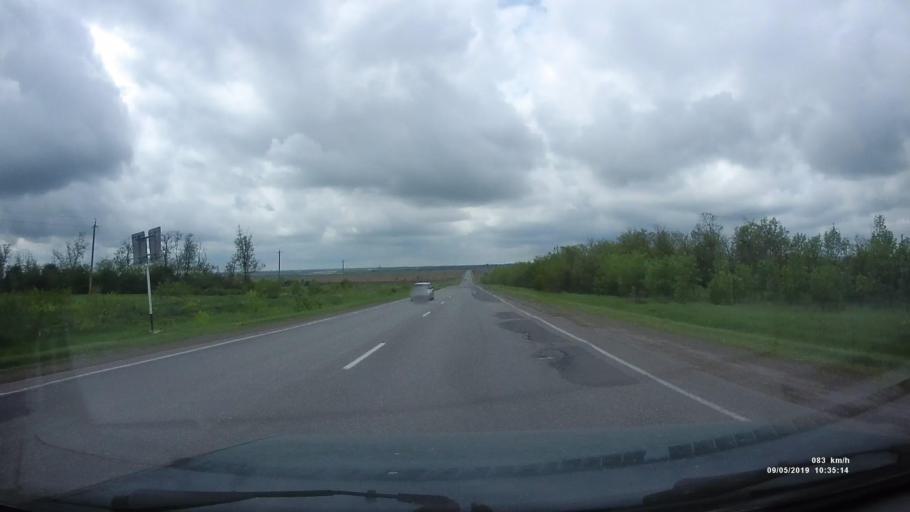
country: RU
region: Rostov
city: Peshkovo
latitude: 47.0456
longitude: 39.4140
